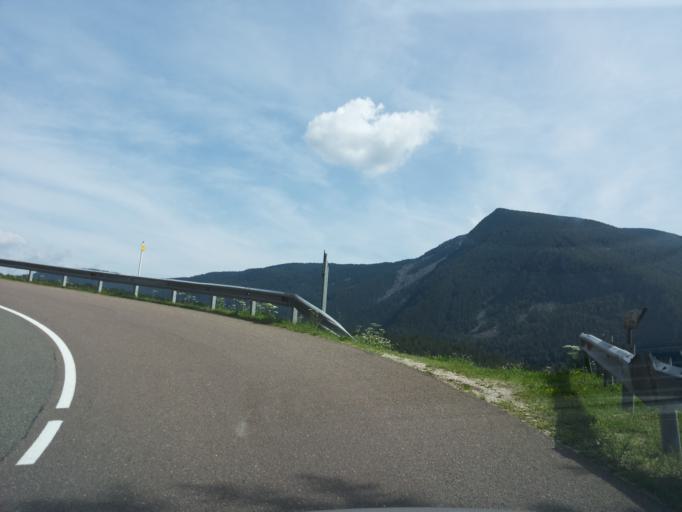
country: IT
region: Trentino-Alto Adige
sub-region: Bolzano
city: Ortisei
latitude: 46.5742
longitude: 11.6311
